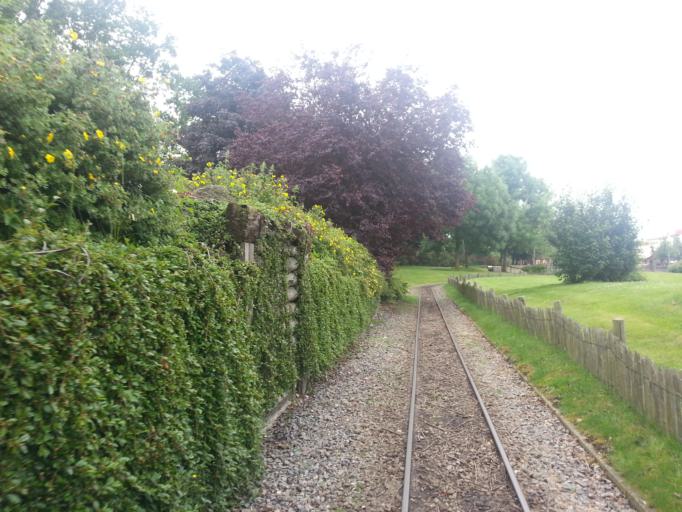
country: DE
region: Schleswig-Holstein
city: Sierksdorf
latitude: 54.0770
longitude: 10.7795
